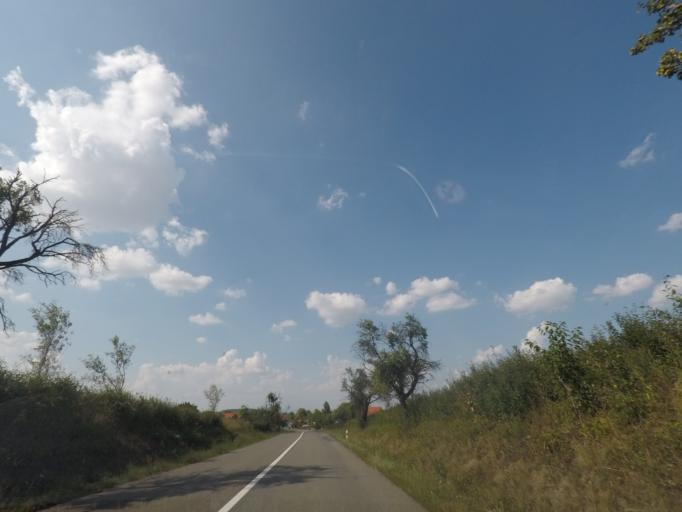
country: CZ
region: Kralovehradecky
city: Dolni Cernilov
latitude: 50.2358
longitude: 15.9689
